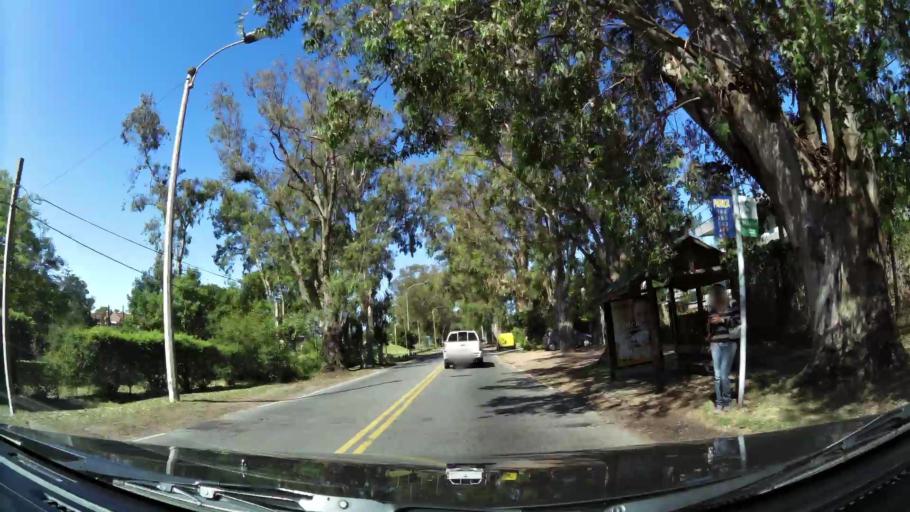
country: UY
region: Canelones
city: Barra de Carrasco
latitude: -34.8811
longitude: -56.0437
